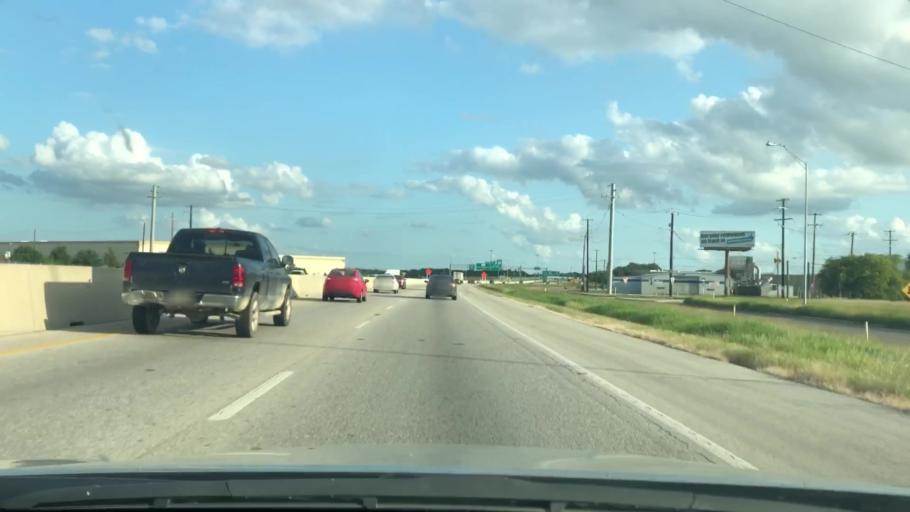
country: US
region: Texas
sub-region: Bexar County
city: Kirby
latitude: 29.4426
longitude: -98.3948
